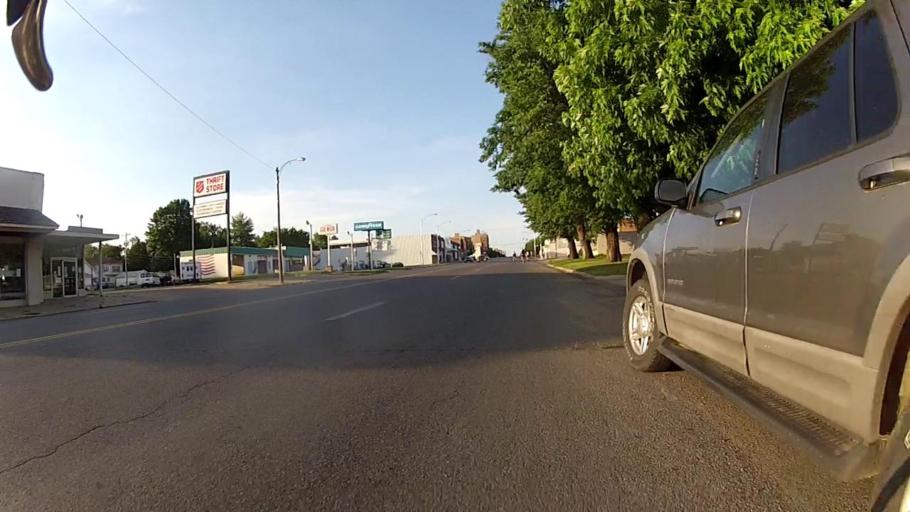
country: US
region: Kansas
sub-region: Cowley County
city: Arkansas City
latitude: 37.0654
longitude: -97.0392
